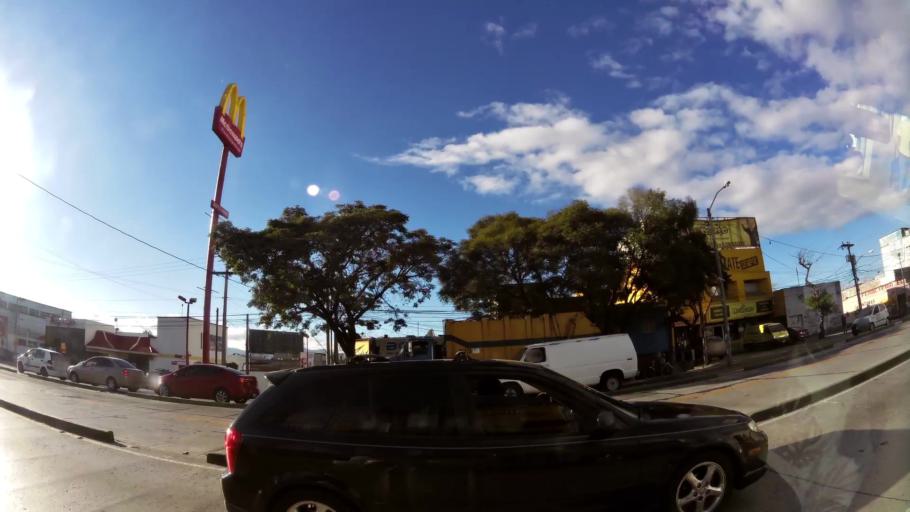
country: GT
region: Guatemala
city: Guatemala City
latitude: 14.6188
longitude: -90.5281
